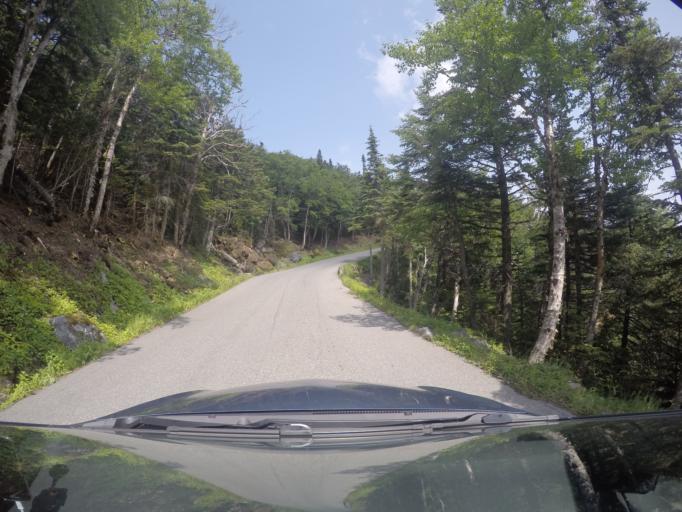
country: US
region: New Hampshire
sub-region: Coos County
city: Gorham
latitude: 44.2901
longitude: -71.2736
